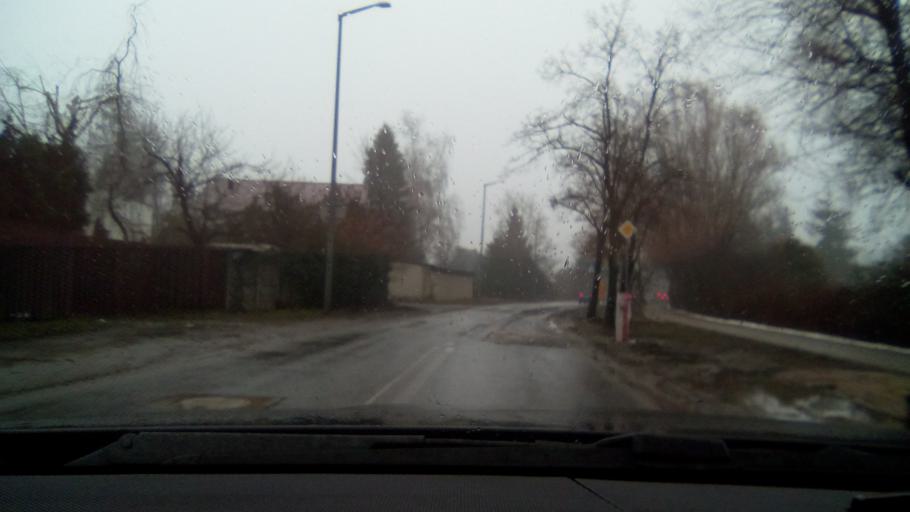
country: PL
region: Greater Poland Voivodeship
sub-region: Powiat poznanski
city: Swarzedz
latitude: 52.3909
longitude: 17.0211
